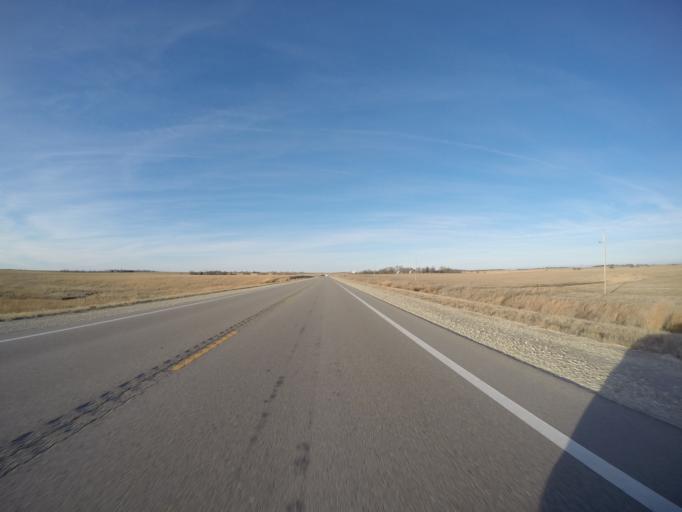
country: US
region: Kansas
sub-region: Marion County
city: Marion
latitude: 38.3421
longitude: -96.9667
